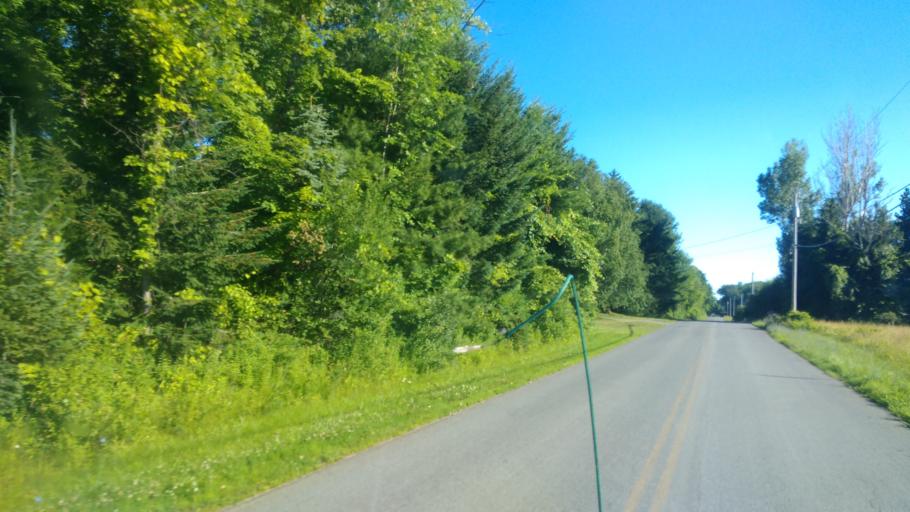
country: US
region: New York
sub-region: Wayne County
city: Sodus
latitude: 43.2514
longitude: -77.1117
